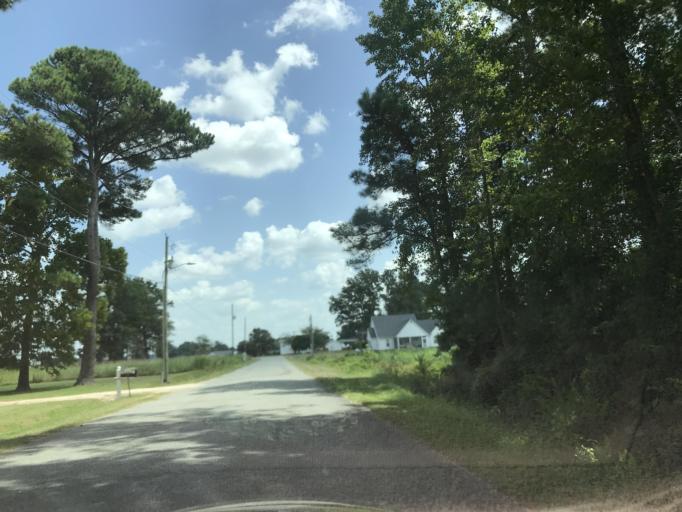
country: US
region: North Carolina
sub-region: Sampson County
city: Plain View
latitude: 35.2481
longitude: -78.3603
